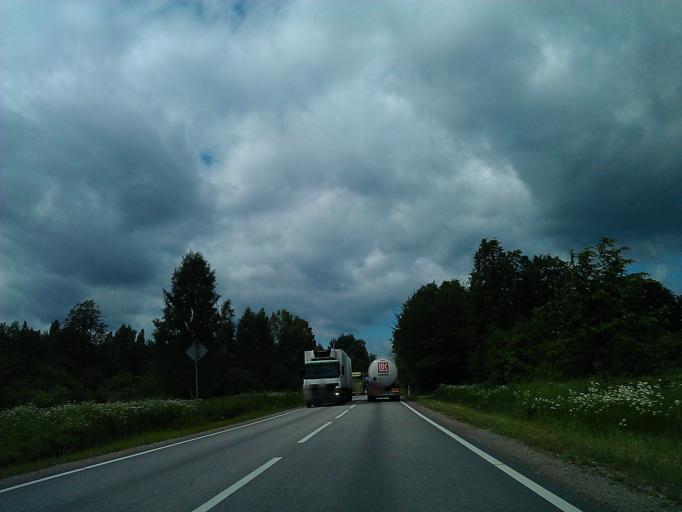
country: LV
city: Tireli
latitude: 56.9265
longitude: 23.5457
